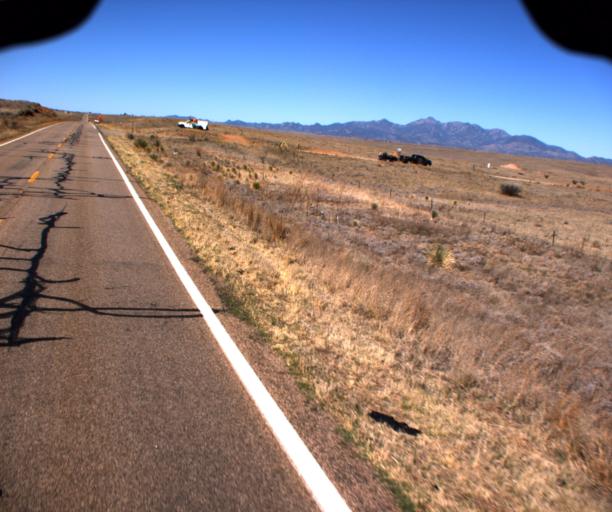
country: US
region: Arizona
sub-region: Cochise County
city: Huachuca City
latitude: 31.7010
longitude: -110.5915
